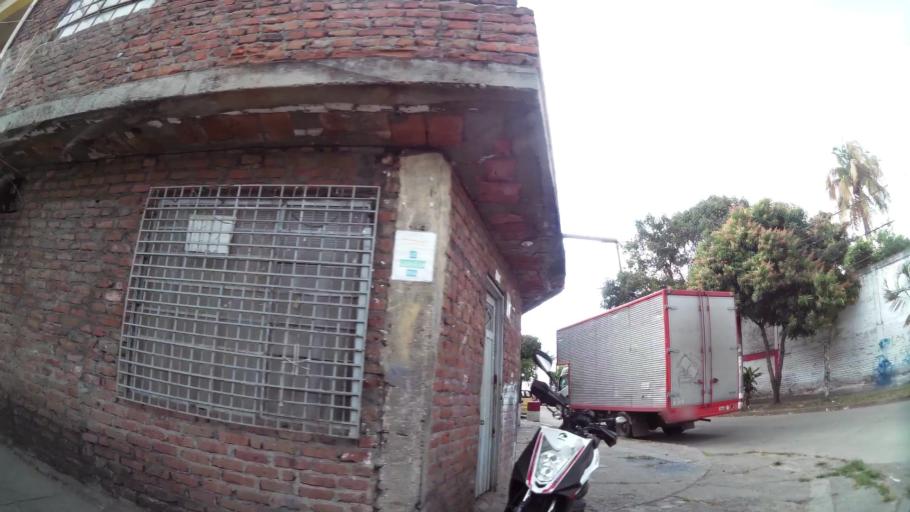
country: CO
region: Valle del Cauca
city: Cali
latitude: 3.4745
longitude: -76.5082
